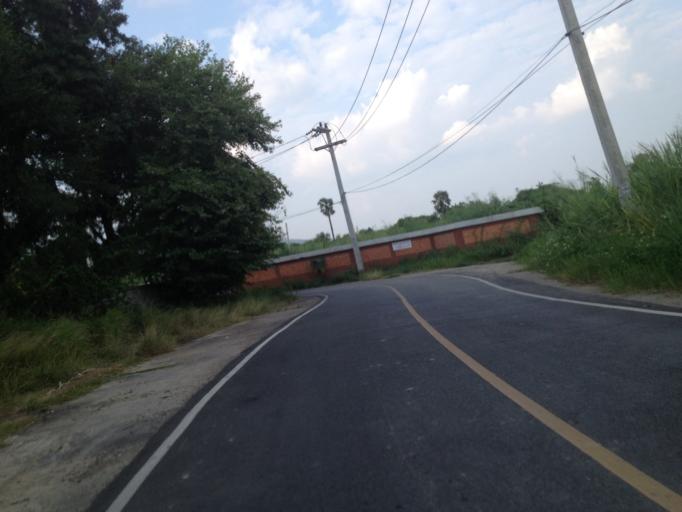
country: TH
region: Chiang Mai
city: Hang Dong
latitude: 18.7458
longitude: 98.9363
